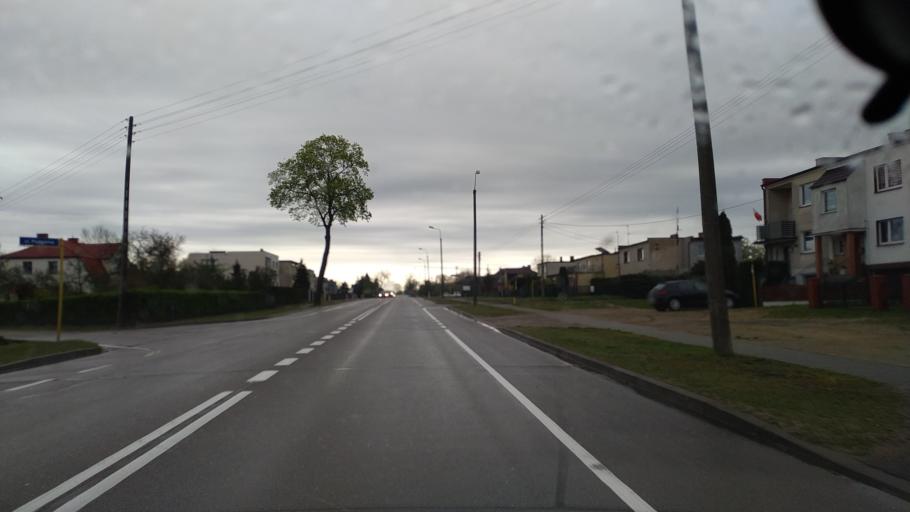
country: PL
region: Pomeranian Voivodeship
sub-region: Powiat chojnicki
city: Czersk
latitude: 53.7986
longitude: 17.9901
